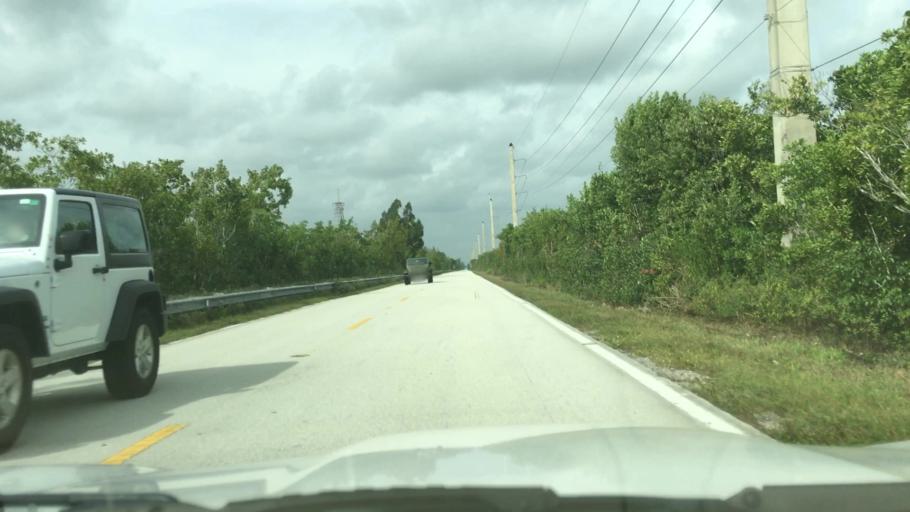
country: US
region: Florida
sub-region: Monroe County
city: North Key Largo
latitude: 25.3203
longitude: -80.3995
